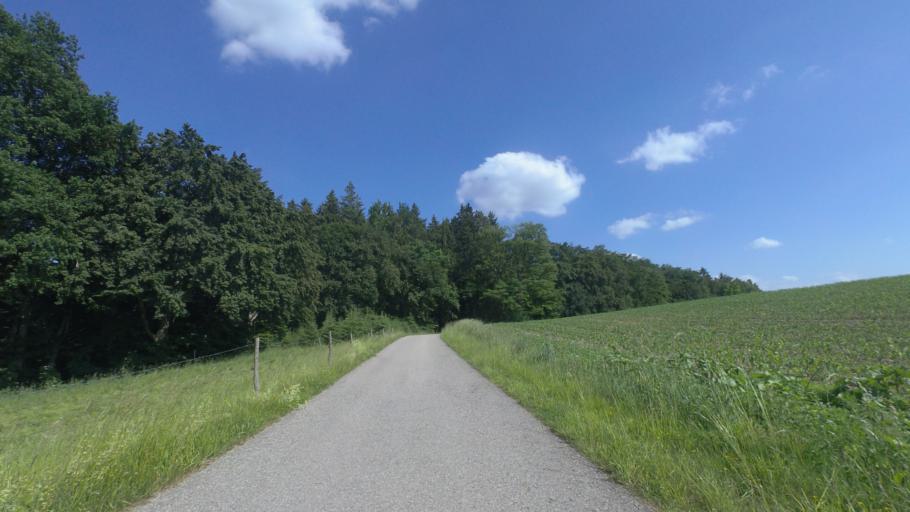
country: DE
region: Bavaria
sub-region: Upper Bavaria
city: Seeon-Seebruck
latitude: 47.9682
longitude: 12.4987
